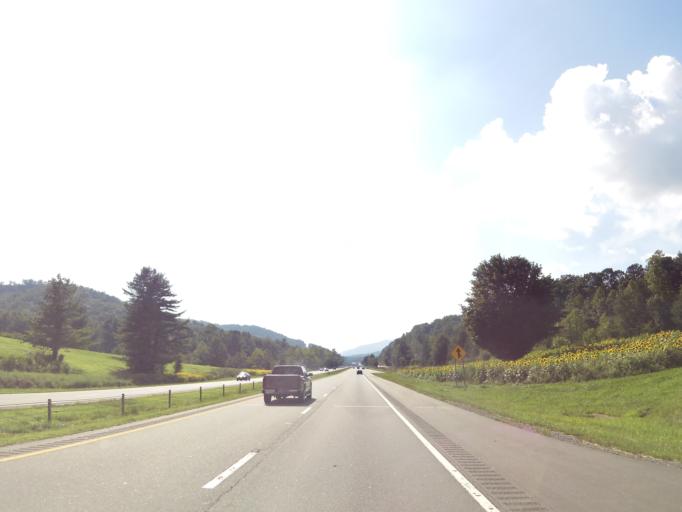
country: US
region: North Carolina
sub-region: Buncombe County
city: Black Mountain
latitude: 35.6193
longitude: -82.2871
